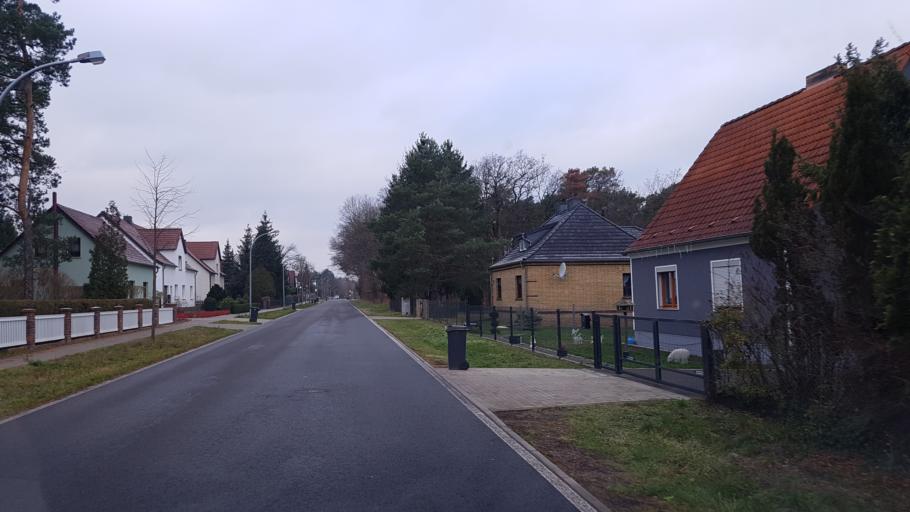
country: DE
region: Brandenburg
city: Sallgast
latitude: 51.5603
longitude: 13.8753
